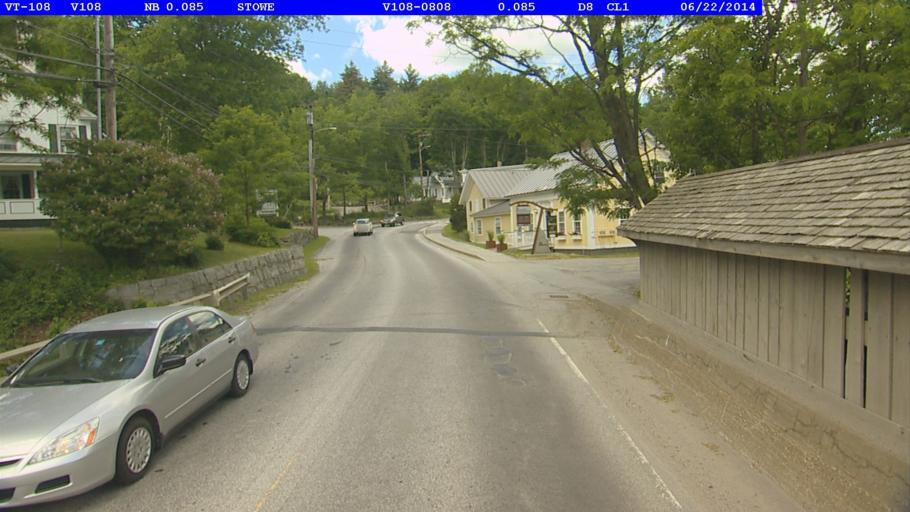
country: US
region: Vermont
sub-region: Lamoille County
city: Morristown
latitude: 44.4666
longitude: -72.6882
